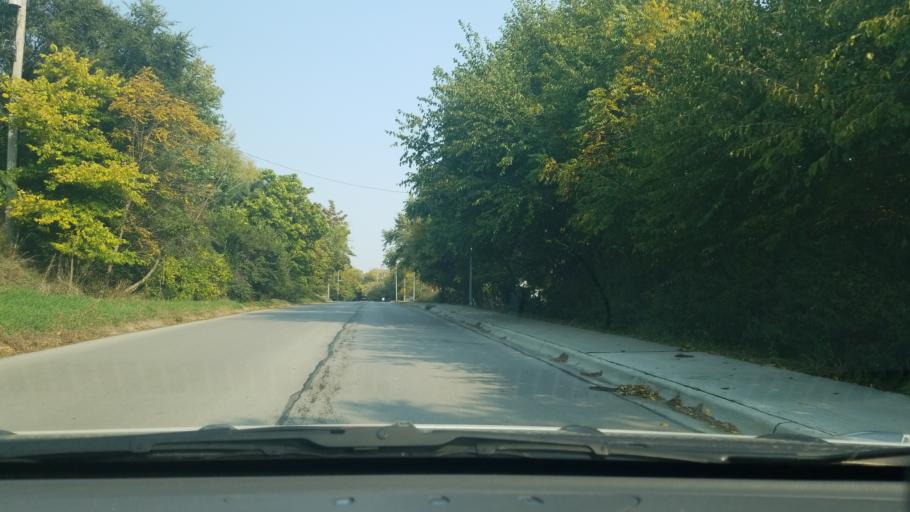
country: US
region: Nebraska
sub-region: Sarpy County
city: Bellevue
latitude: 41.1572
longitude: -95.9091
